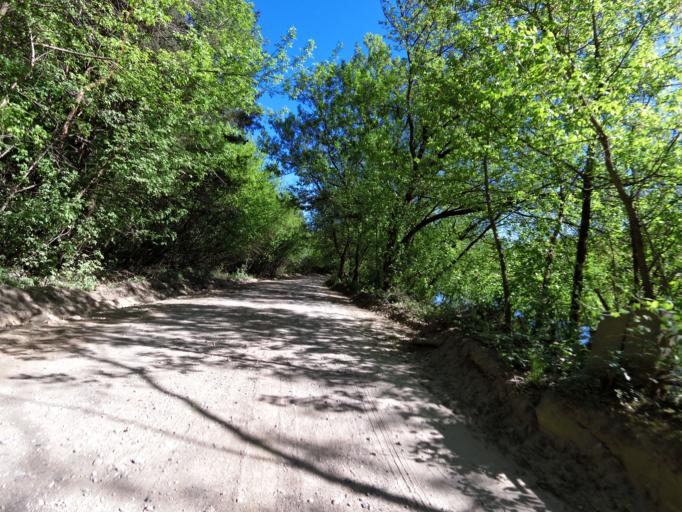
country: LT
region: Vilnius County
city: Pilaite
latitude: 54.6799
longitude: 25.1617
